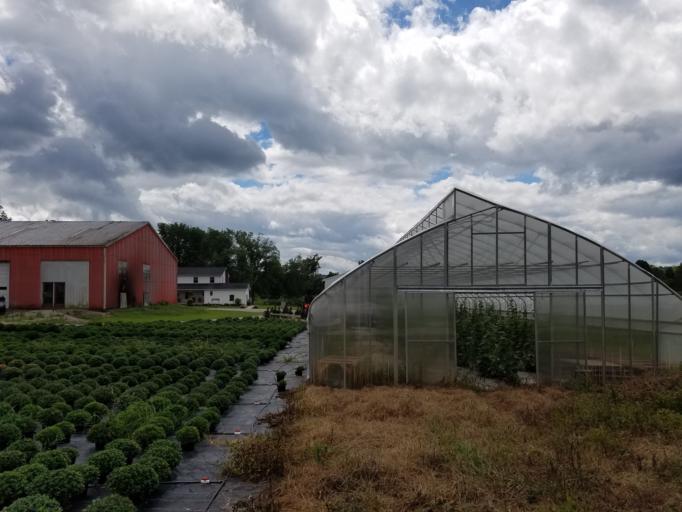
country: US
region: Ohio
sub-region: Gallia County
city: Gallipolis
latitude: 38.8194
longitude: -82.3672
